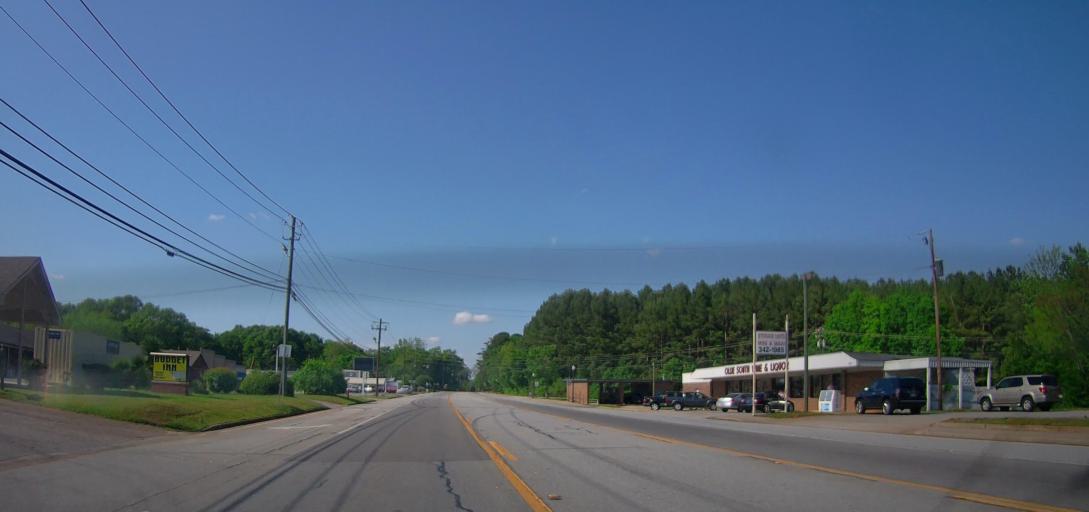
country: US
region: Georgia
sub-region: Morgan County
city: Madison
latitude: 33.5802
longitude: -83.4776
